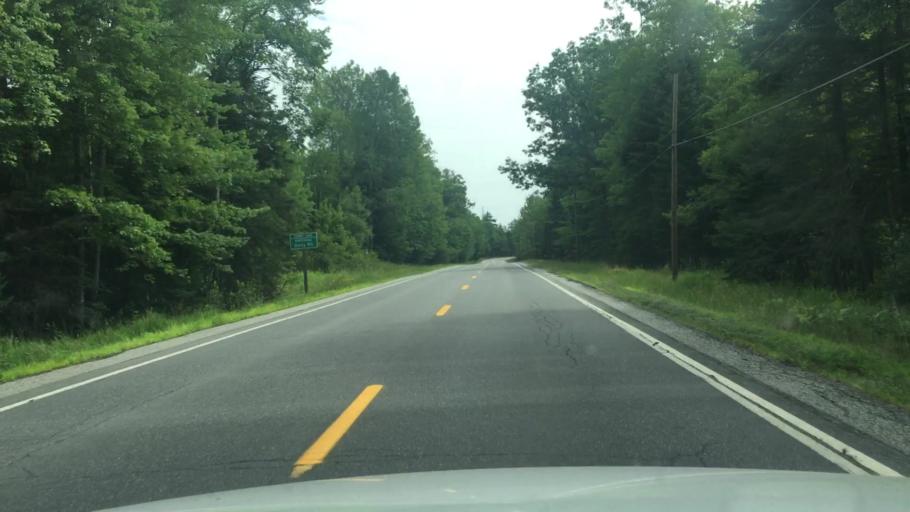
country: US
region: Maine
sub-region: Kennebec County
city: Clinton
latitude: 44.6134
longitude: -69.4366
